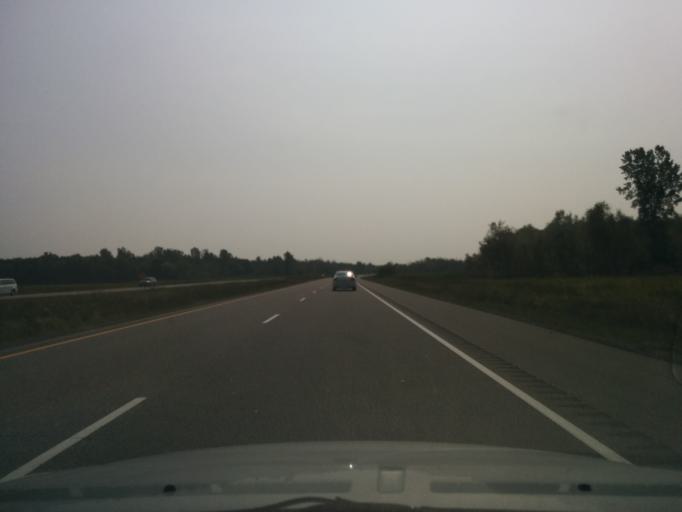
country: CA
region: Ontario
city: Bells Corners
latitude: 45.1076
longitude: -75.6644
